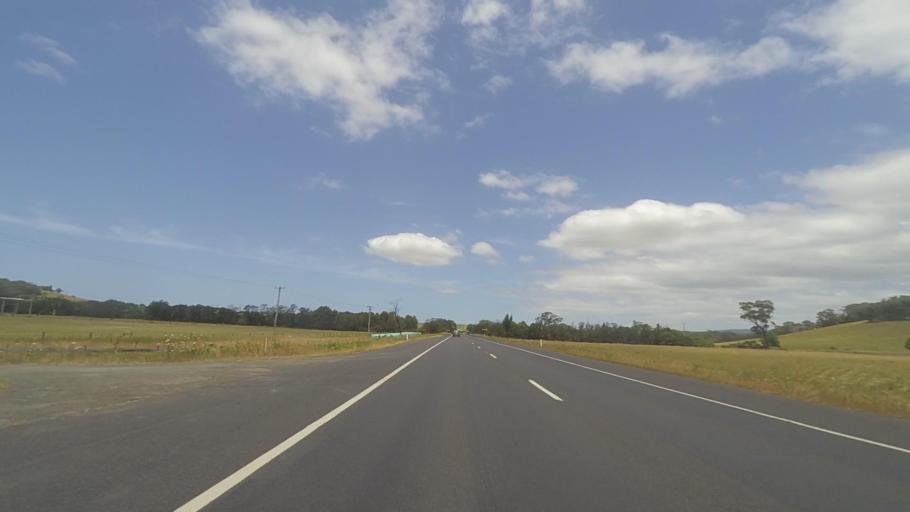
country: AU
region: New South Wales
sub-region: Shoalhaven Shire
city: Milton
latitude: -35.2723
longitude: 150.4240
